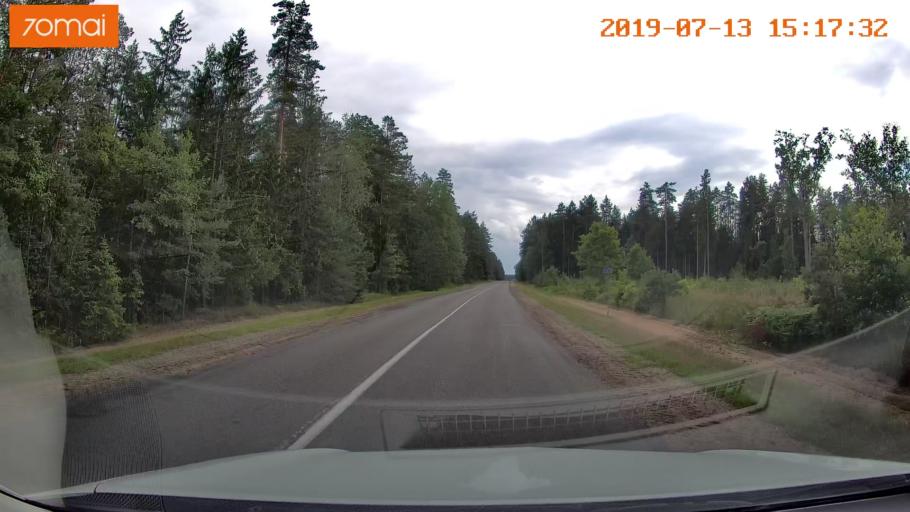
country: BY
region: Mogilev
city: Hlusha
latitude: 53.0948
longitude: 28.8451
